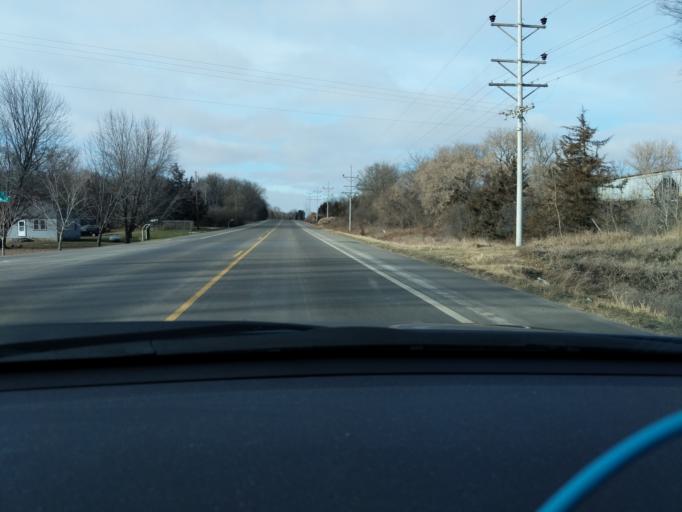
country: US
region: Minnesota
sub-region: Chippewa County
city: Montevideo
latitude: 44.9208
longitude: -95.7000
